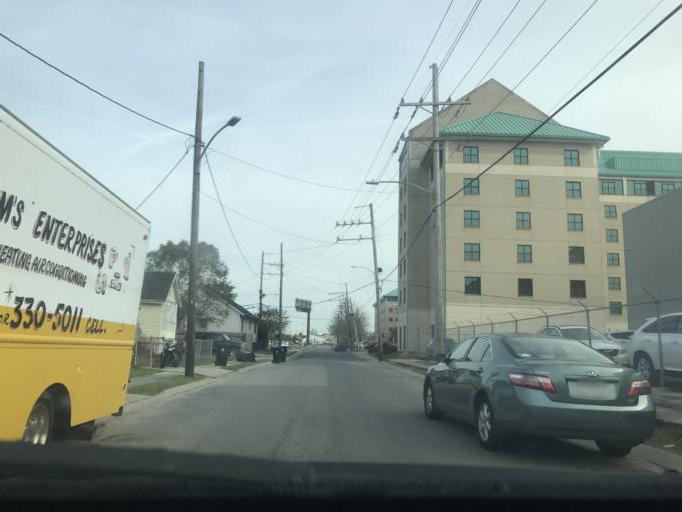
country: US
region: Louisiana
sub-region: Orleans Parish
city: New Orleans
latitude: 29.9607
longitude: -90.1038
